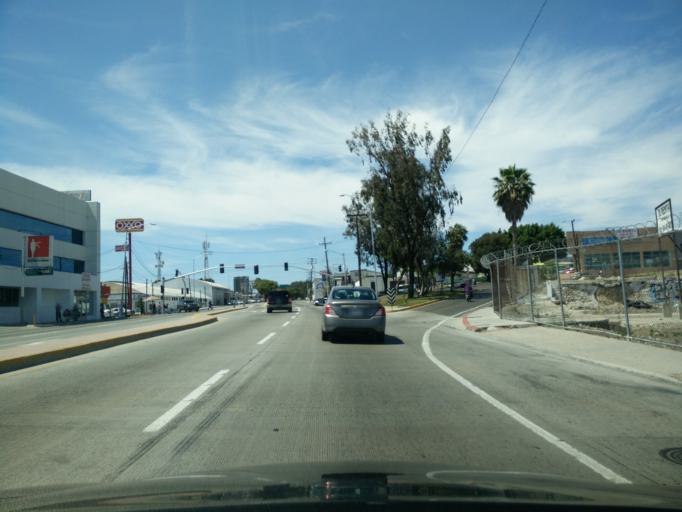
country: MX
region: Baja California
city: Tijuana
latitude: 32.5407
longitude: -116.9973
